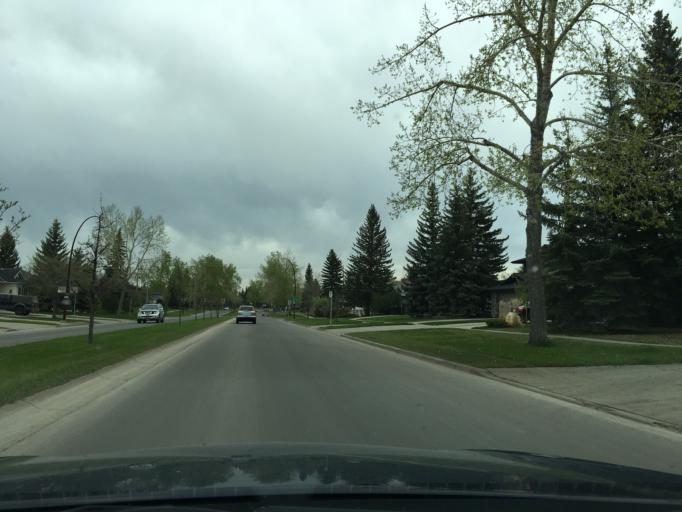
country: CA
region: Alberta
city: Calgary
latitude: 50.9358
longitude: -114.0647
